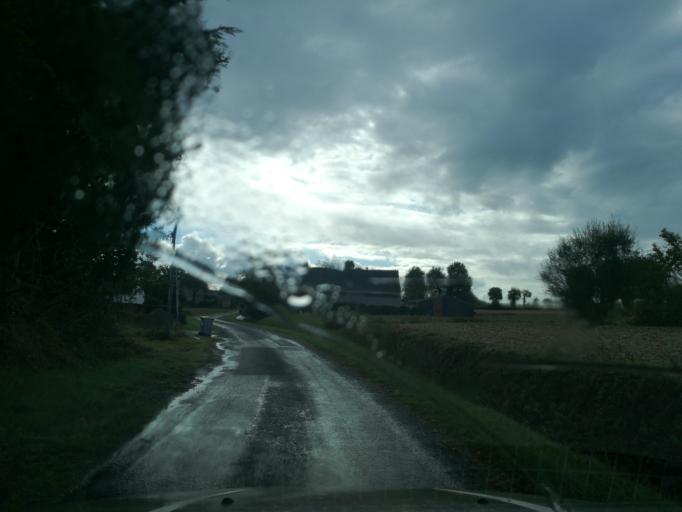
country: FR
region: Brittany
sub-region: Departement d'Ille-et-Vilaine
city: Bedee
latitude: 48.2006
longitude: -1.9895
